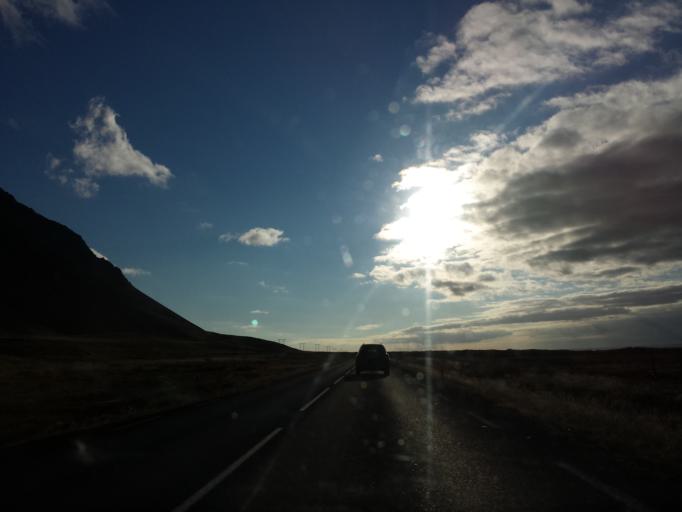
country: IS
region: West
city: Borgarnes
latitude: 64.5062
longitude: -21.9231
